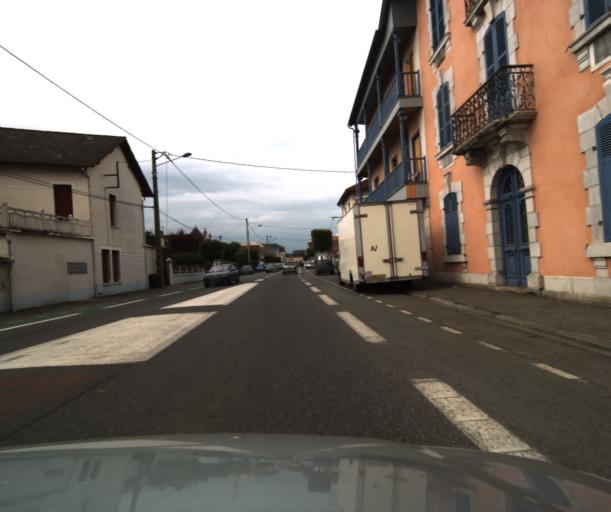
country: FR
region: Midi-Pyrenees
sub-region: Departement des Hautes-Pyrenees
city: Aureilhan
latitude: 43.2358
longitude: 0.0928
